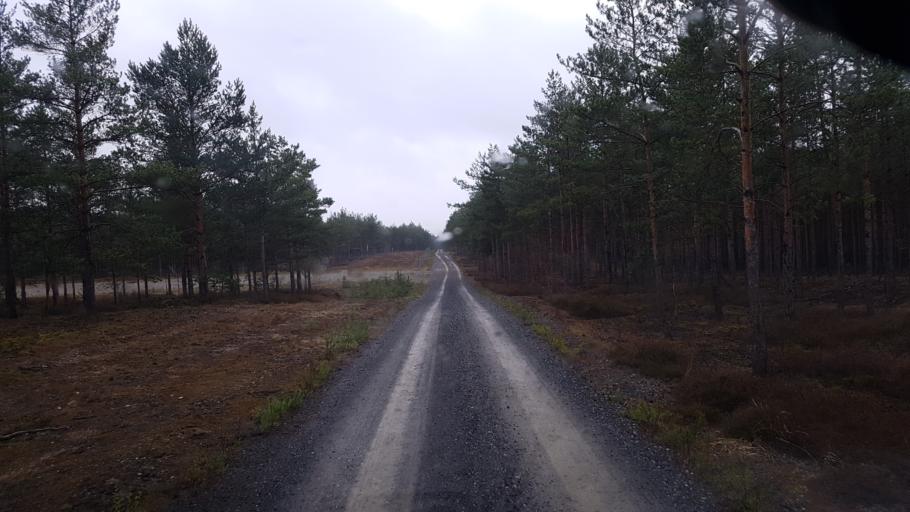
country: DE
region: Brandenburg
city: Grossraschen
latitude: 51.6131
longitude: 13.9619
